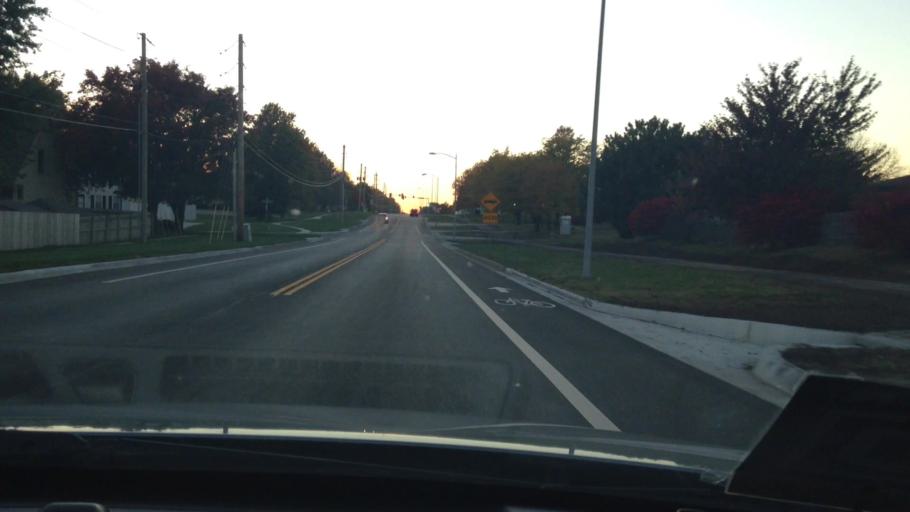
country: US
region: Kansas
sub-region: Johnson County
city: Olathe
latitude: 38.8691
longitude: -94.7572
